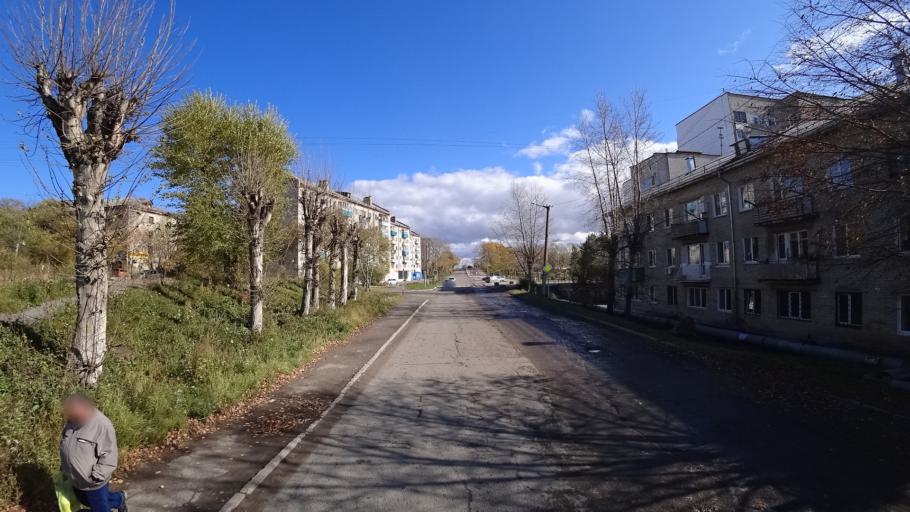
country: RU
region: Khabarovsk Krai
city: Amursk
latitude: 50.2149
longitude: 136.9006
